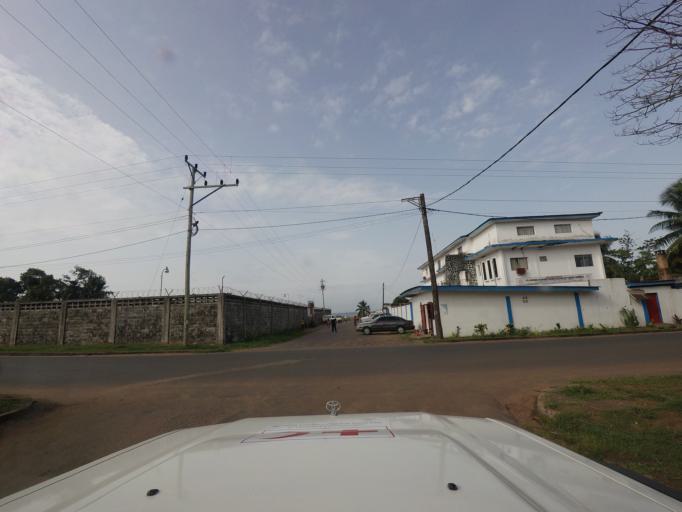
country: LR
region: Montserrado
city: Monrovia
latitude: 6.2889
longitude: -10.7769
